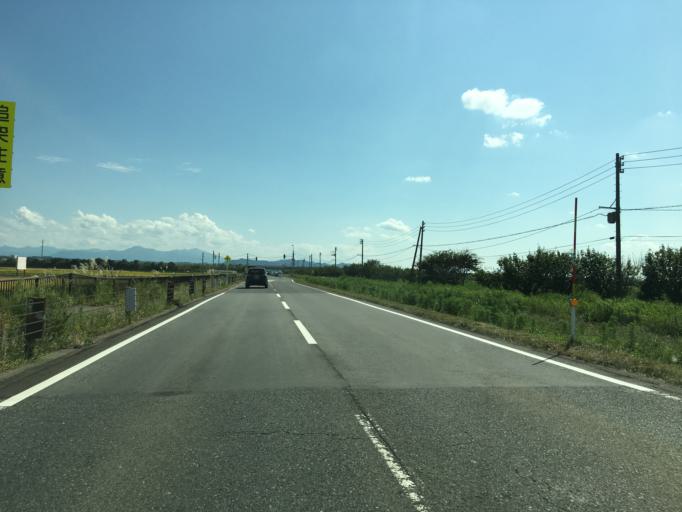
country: JP
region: Niigata
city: Niitsu-honcho
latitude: 37.8268
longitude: 139.0979
